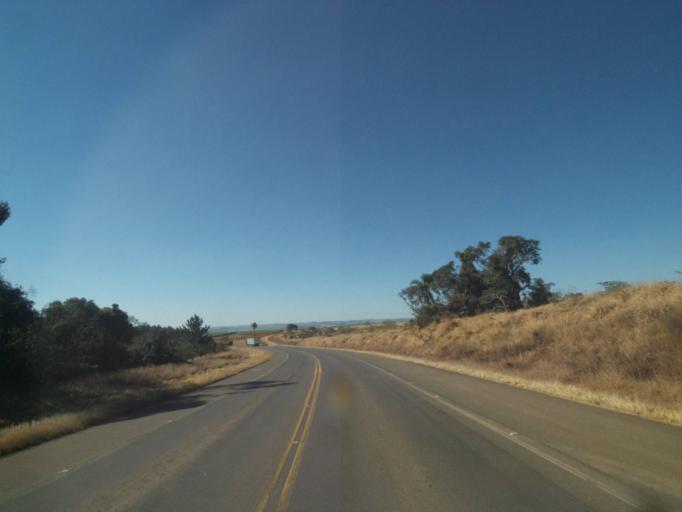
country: BR
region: Parana
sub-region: Tibagi
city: Tibagi
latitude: -24.6949
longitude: -50.4427
